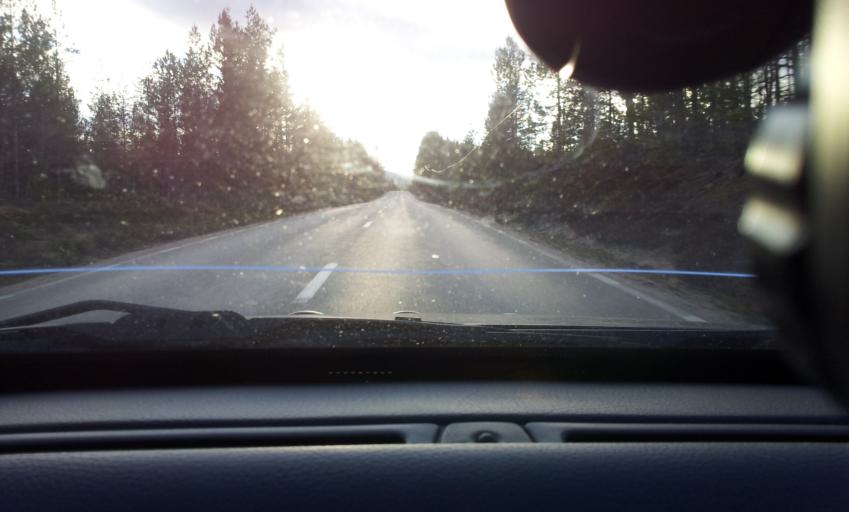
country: SE
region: Jaemtland
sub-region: Harjedalens Kommun
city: Sveg
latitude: 62.1237
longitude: 15.0042
